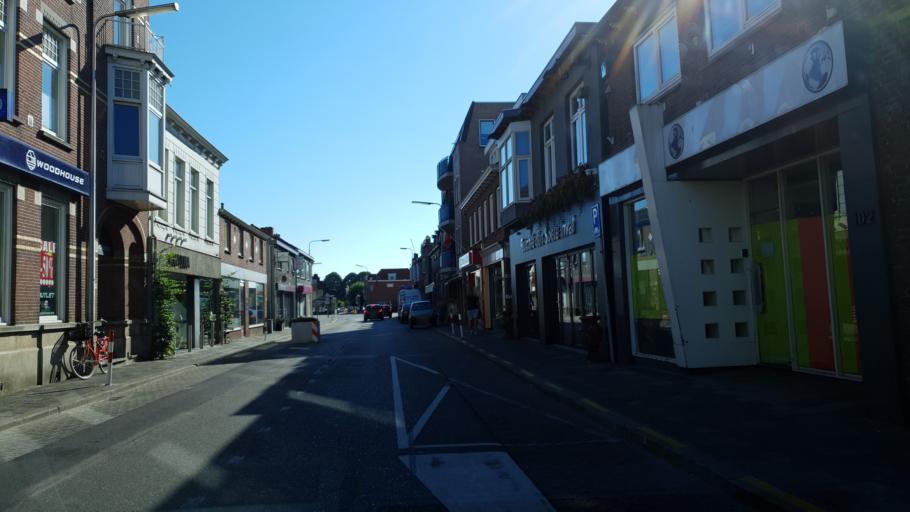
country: NL
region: North Brabant
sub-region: Gemeente Zundert
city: Zundert
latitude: 51.4701
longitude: 4.6598
